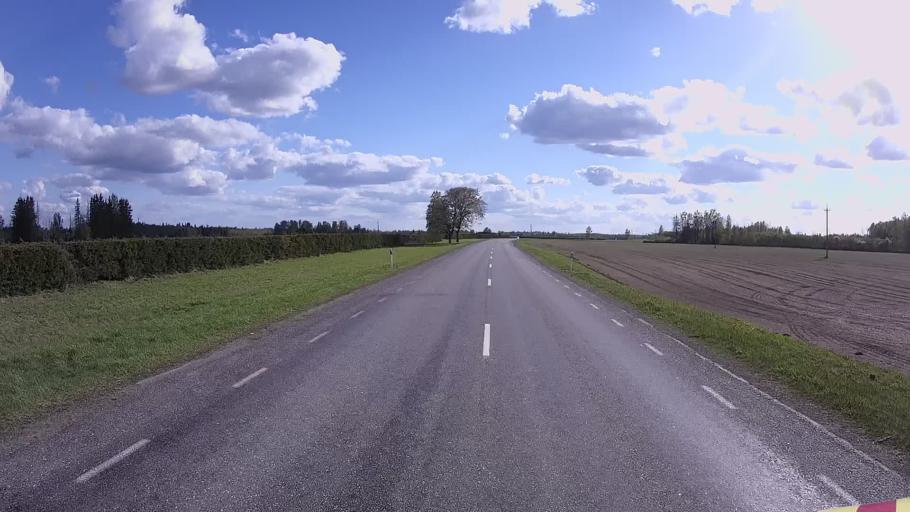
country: EE
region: Jogevamaa
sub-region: Poltsamaa linn
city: Poltsamaa
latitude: 58.6943
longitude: 26.1351
